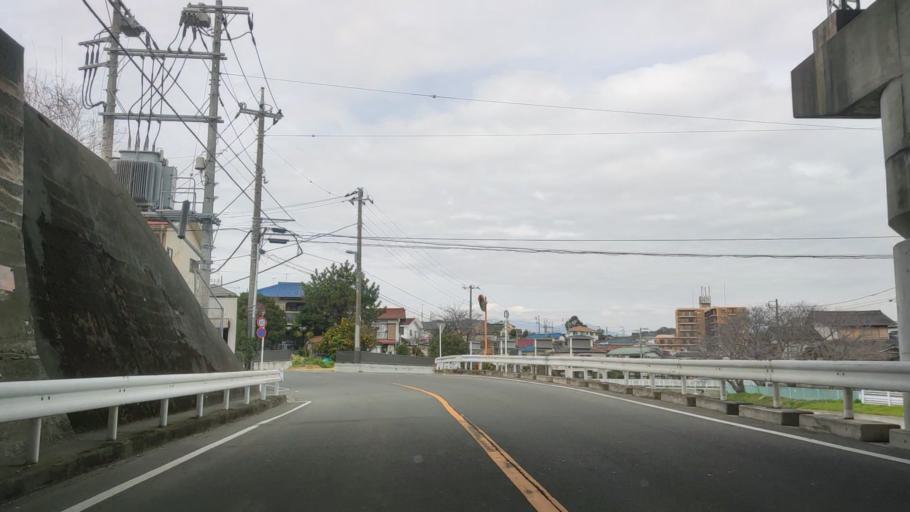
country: JP
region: Kanagawa
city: Ninomiya
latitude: 35.2913
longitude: 139.2354
